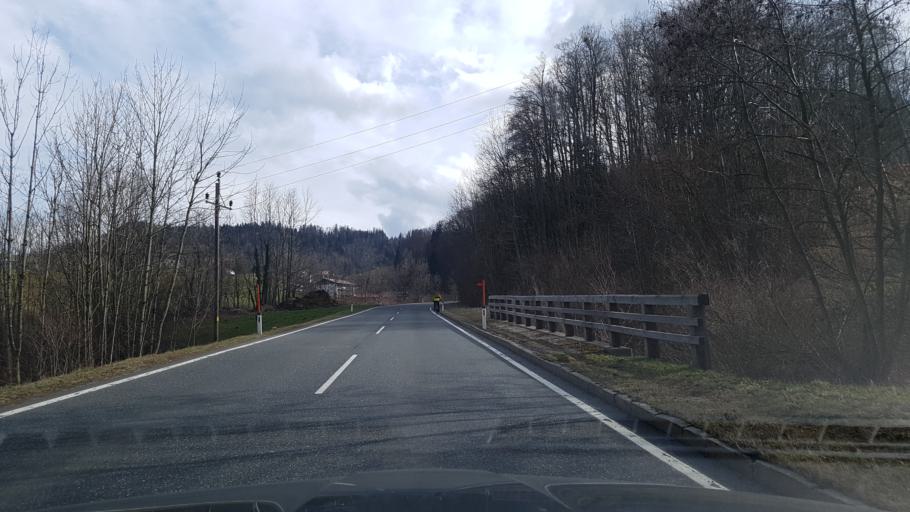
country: AT
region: Salzburg
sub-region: Politischer Bezirk Hallein
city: Hallein
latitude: 47.6657
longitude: 13.0938
